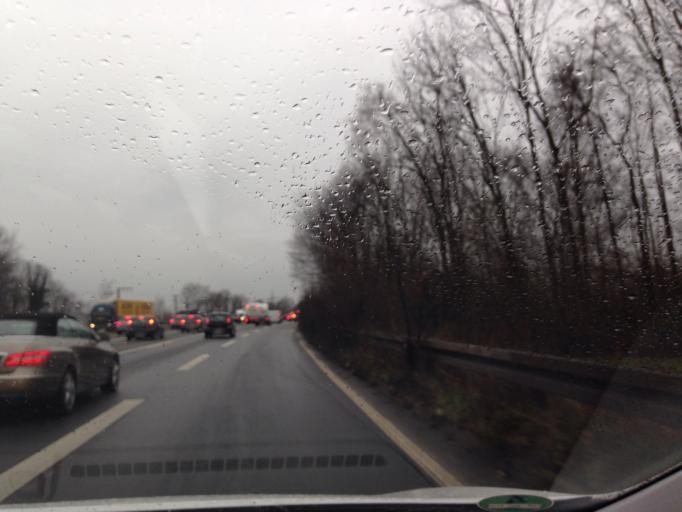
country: DE
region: North Rhine-Westphalia
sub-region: Regierungsbezirk Dusseldorf
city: Duisburg
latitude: 51.4425
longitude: 6.8020
